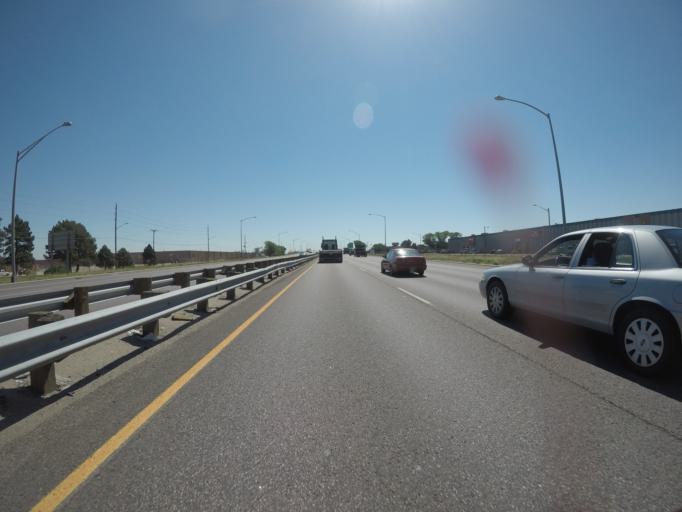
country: US
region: Colorado
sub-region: Adams County
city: Commerce City
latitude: 39.7784
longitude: -104.9171
